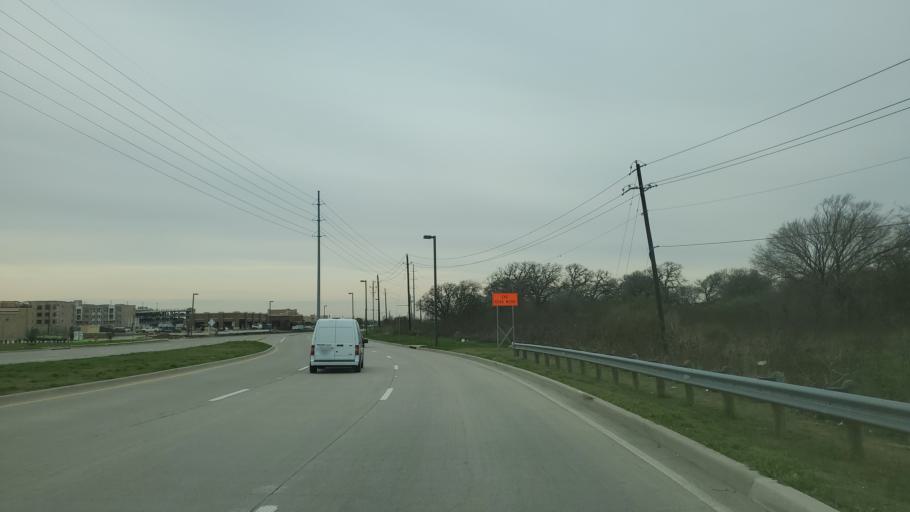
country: US
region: Texas
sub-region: Dallas County
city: Coppell
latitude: 32.9733
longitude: -97.0295
